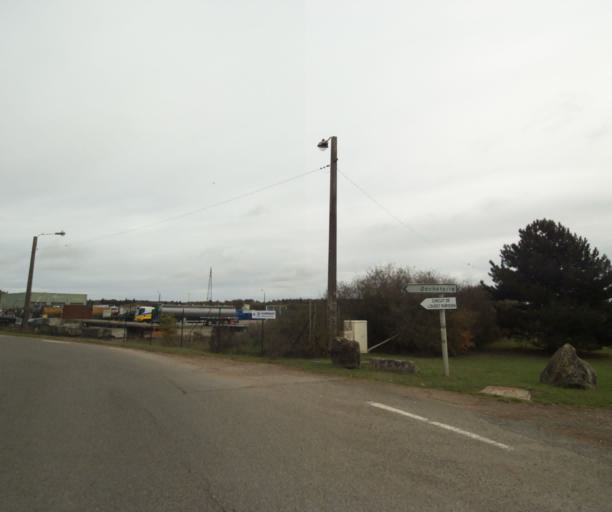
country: FR
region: Centre
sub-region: Departement d'Eure-et-Loir
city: Dreux
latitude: 48.7535
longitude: 1.3672
